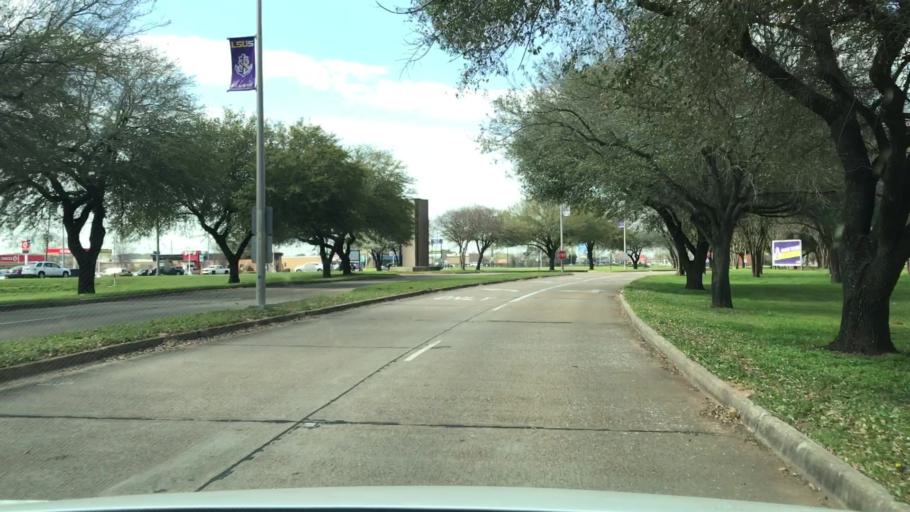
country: US
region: Louisiana
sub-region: Bossier Parish
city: Bossier City
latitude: 32.4262
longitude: -93.7077
